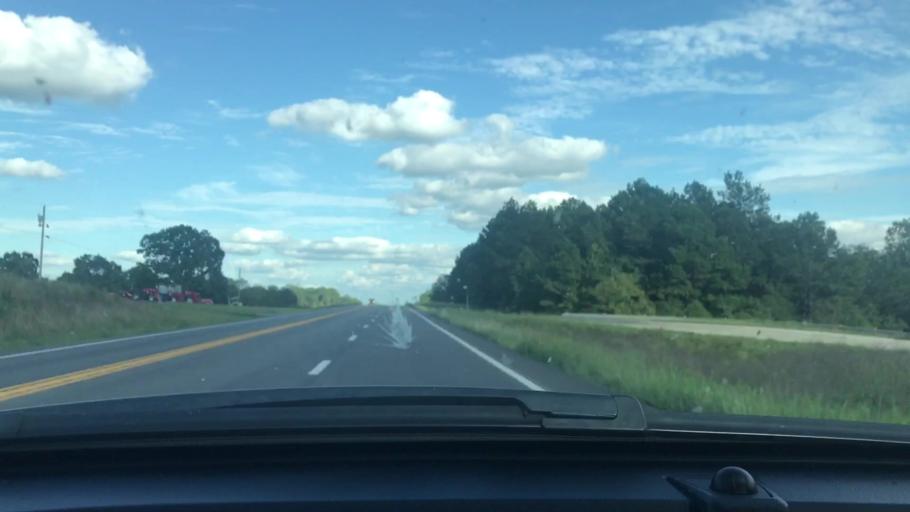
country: US
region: Missouri
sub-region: Oregon County
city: Thayer
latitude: 36.5833
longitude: -91.6127
